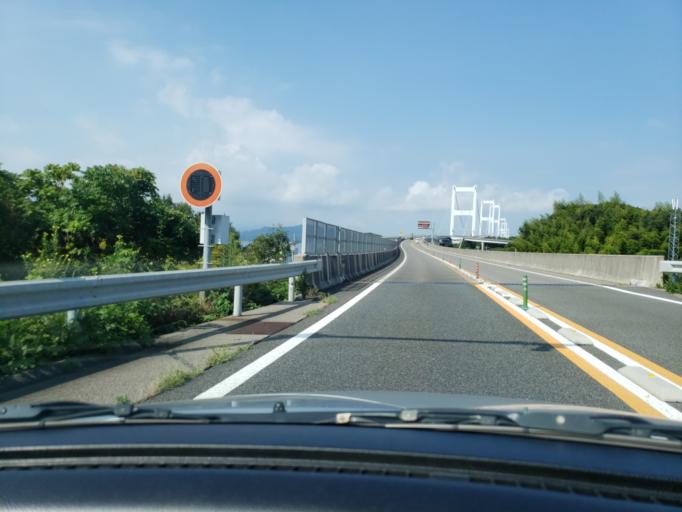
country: JP
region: Hiroshima
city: Innoshima
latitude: 34.1301
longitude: 133.0221
